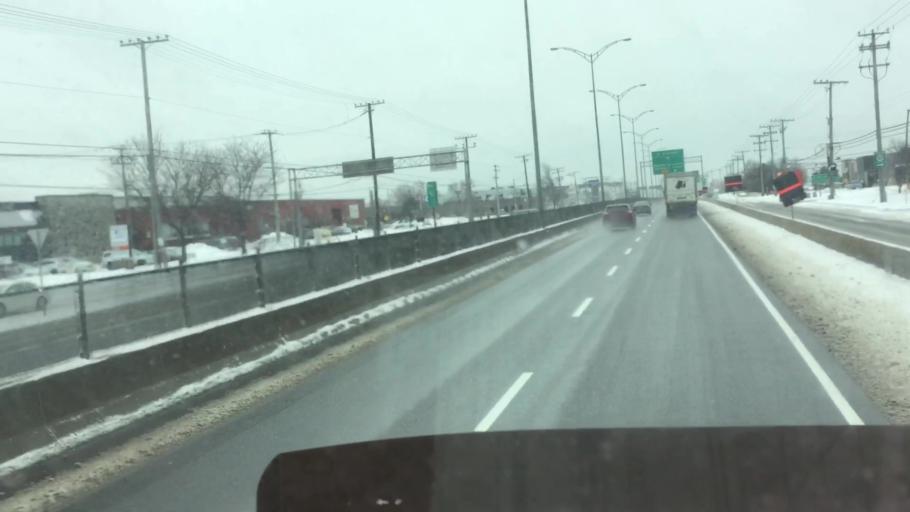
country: CA
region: Quebec
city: Hampstead
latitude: 45.4830
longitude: -73.6954
